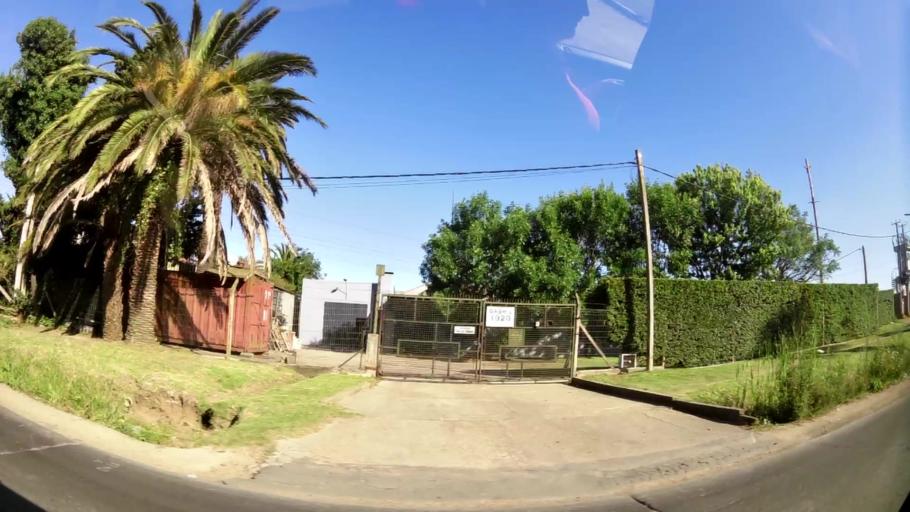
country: UY
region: Montevideo
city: Montevideo
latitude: -34.8288
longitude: -56.1847
